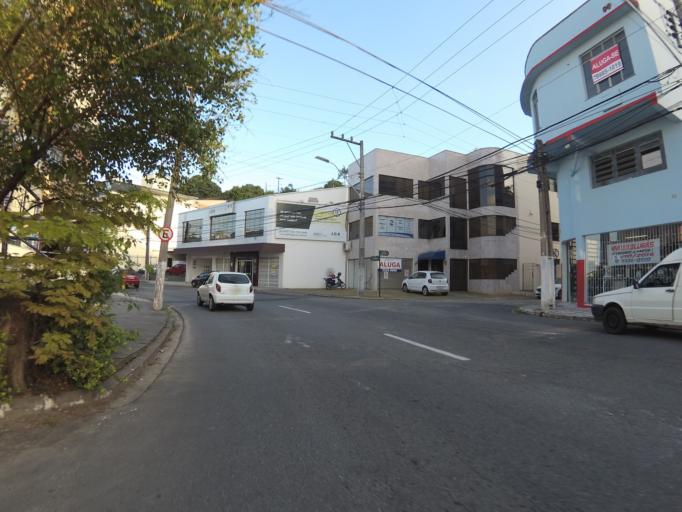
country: BR
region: Santa Catarina
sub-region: Blumenau
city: Blumenau
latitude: -26.9143
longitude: -49.0772
